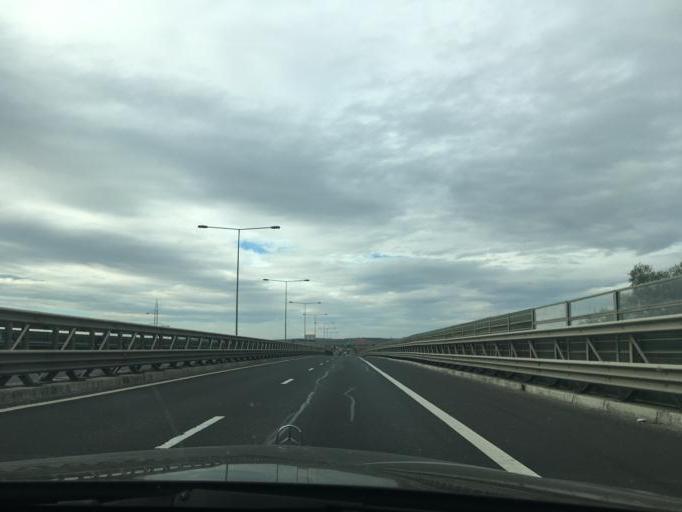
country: RO
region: Sibiu
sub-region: Municipiul Sibiu
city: Sibiu
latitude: 45.8084
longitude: 24.1755
